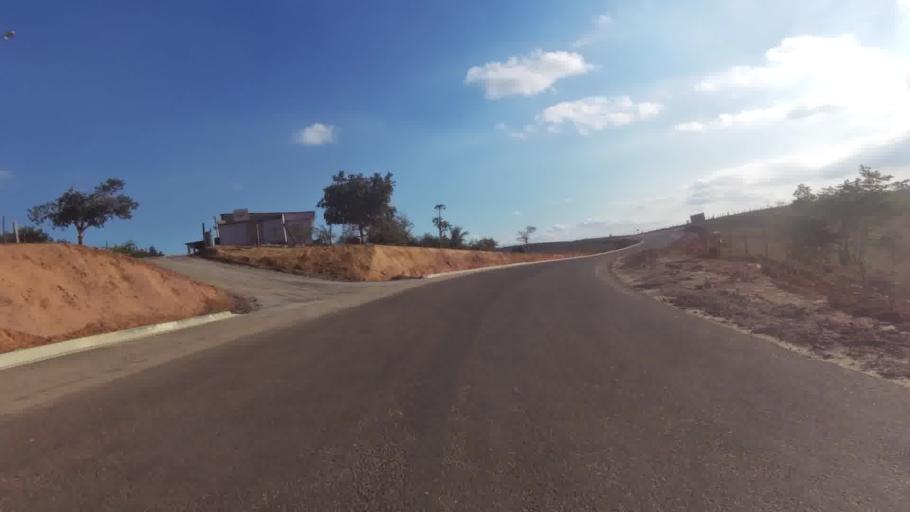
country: BR
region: Espirito Santo
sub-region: Marataizes
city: Marataizes
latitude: -21.1450
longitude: -41.0654
